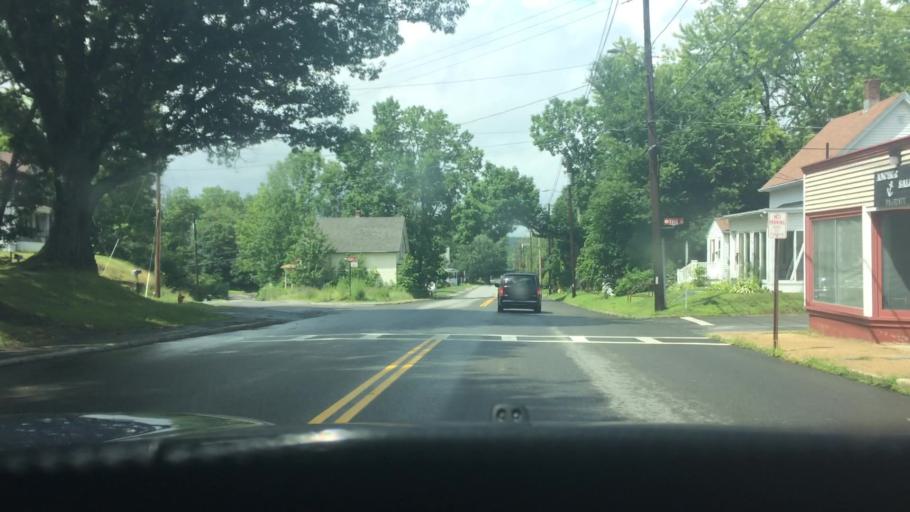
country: US
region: Massachusetts
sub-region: Worcester County
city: Gardner
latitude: 42.5747
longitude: -72.0086
